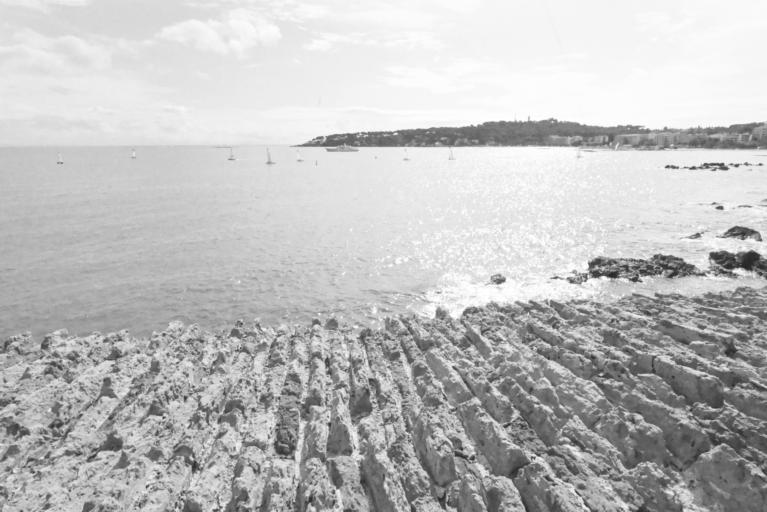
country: FR
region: Provence-Alpes-Cote d'Azur
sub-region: Departement des Alpes-Maritimes
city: Antibes
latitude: 43.5784
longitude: 7.1268
